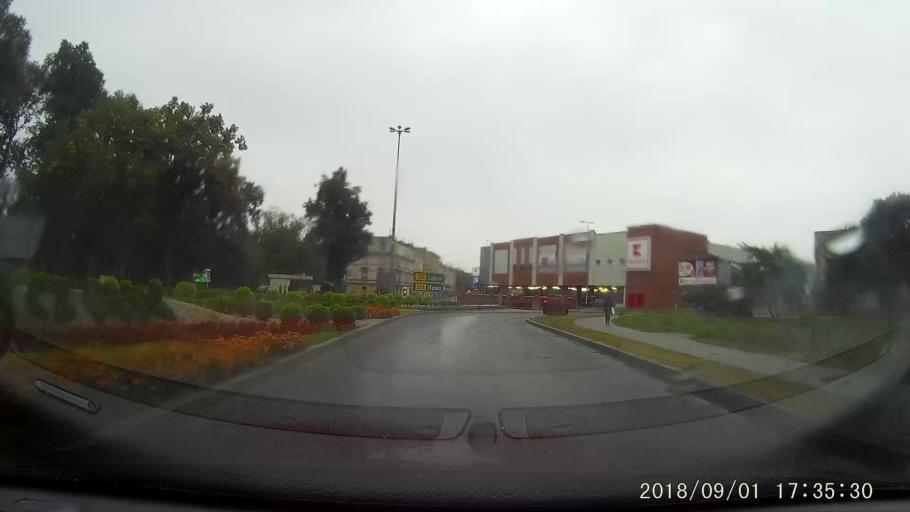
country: PL
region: Lubusz
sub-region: Powiat zaganski
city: Zagan
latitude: 51.6177
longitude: 15.3145
